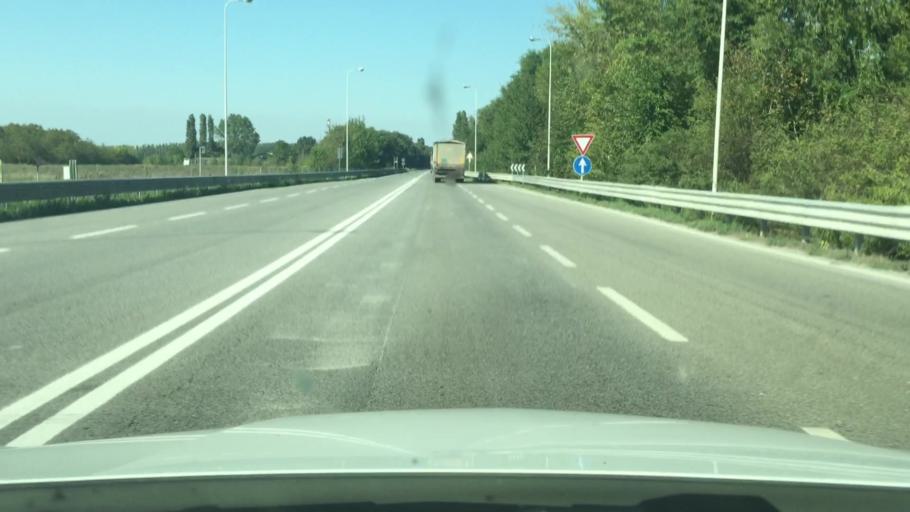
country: IT
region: Emilia-Romagna
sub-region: Provincia di Ravenna
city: Ravenna
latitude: 44.4614
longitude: 12.2089
